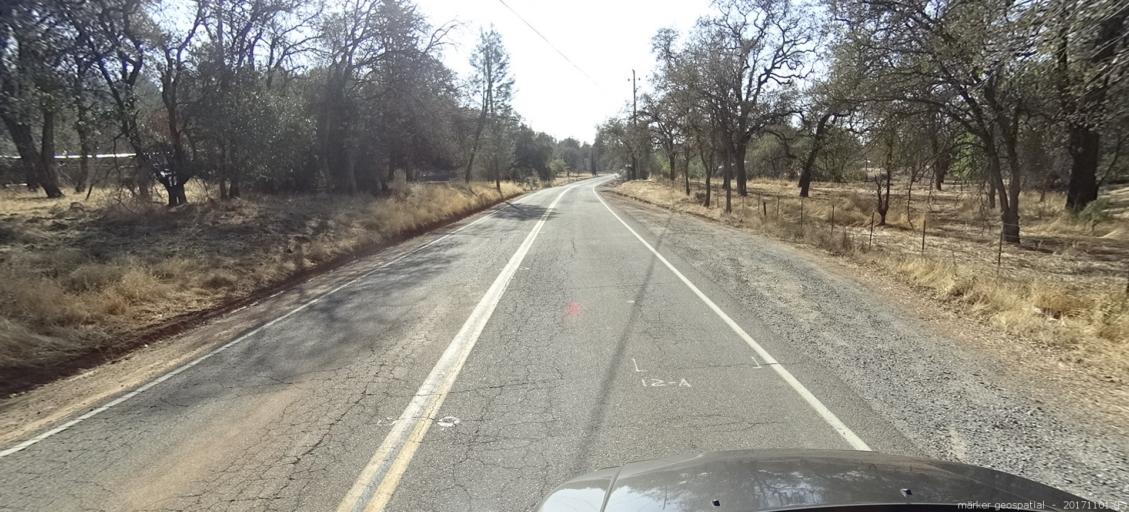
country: US
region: California
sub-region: Shasta County
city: Shasta Lake
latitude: 40.6949
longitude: -122.3184
